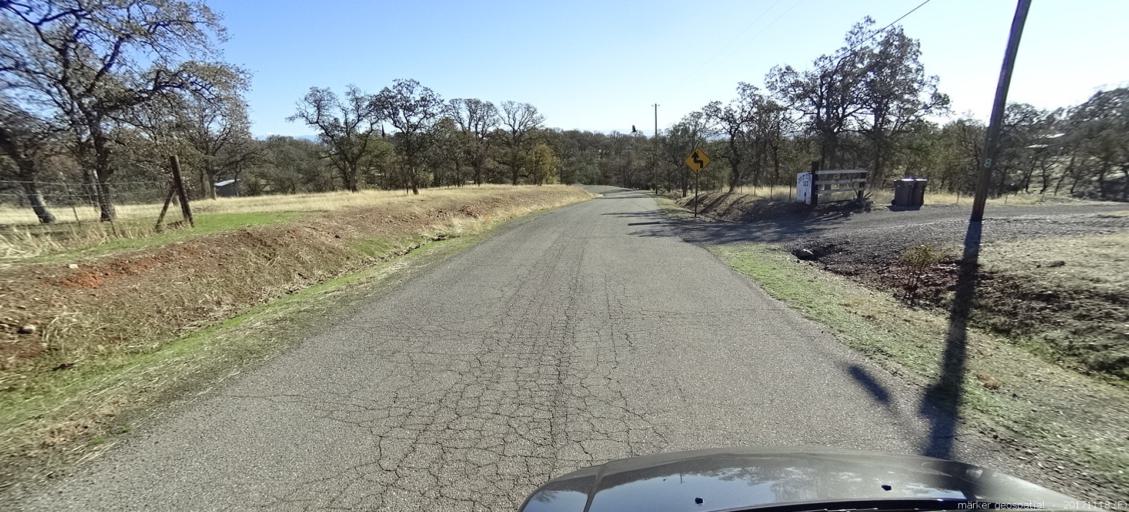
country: US
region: California
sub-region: Shasta County
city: Cottonwood
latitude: 40.3948
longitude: -122.3229
